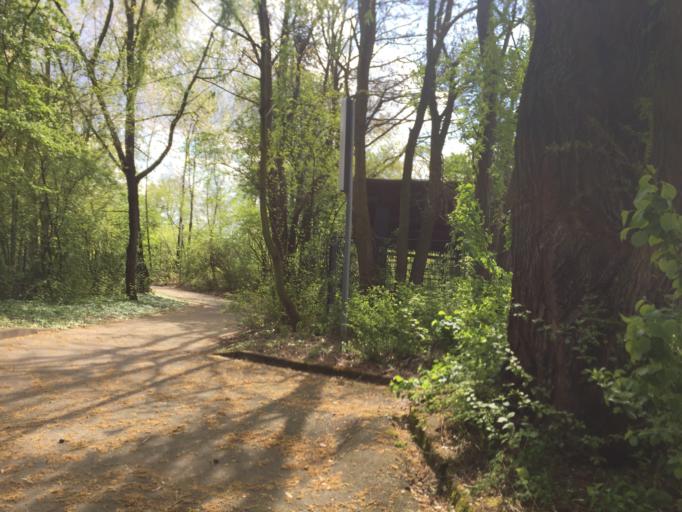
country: DE
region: North Rhine-Westphalia
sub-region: Regierungsbezirk Koln
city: Bonn
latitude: 50.7481
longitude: 7.0750
